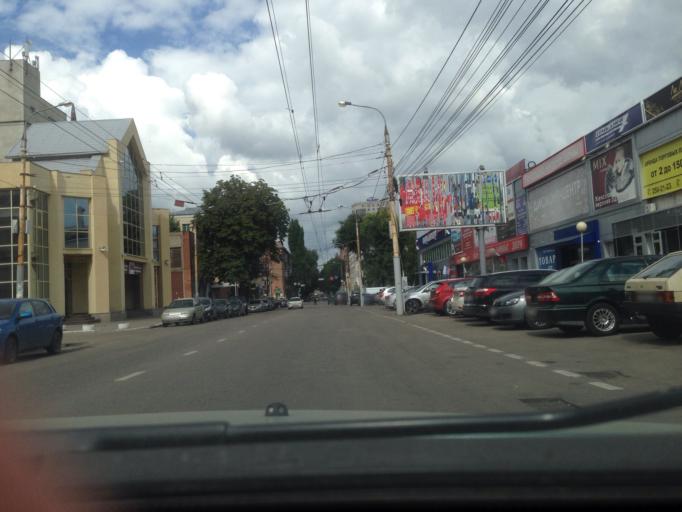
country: RU
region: Voronezj
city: Voronezh
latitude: 51.6687
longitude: 39.1960
